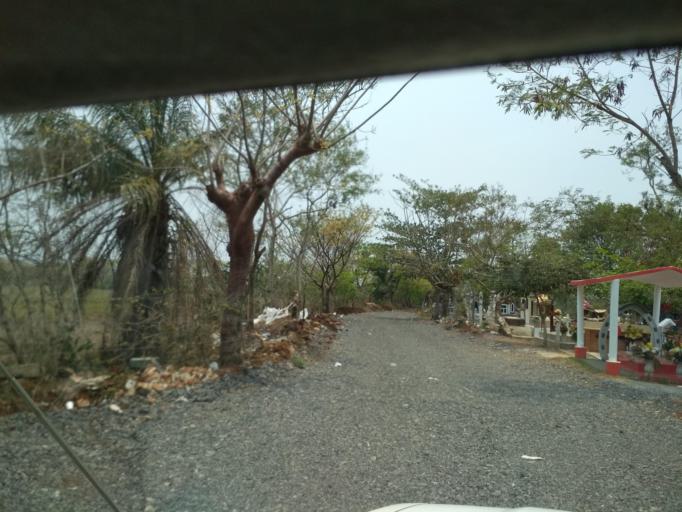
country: MX
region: Veracruz
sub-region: Veracruz
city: Oasis
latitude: 19.1958
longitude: -96.2441
